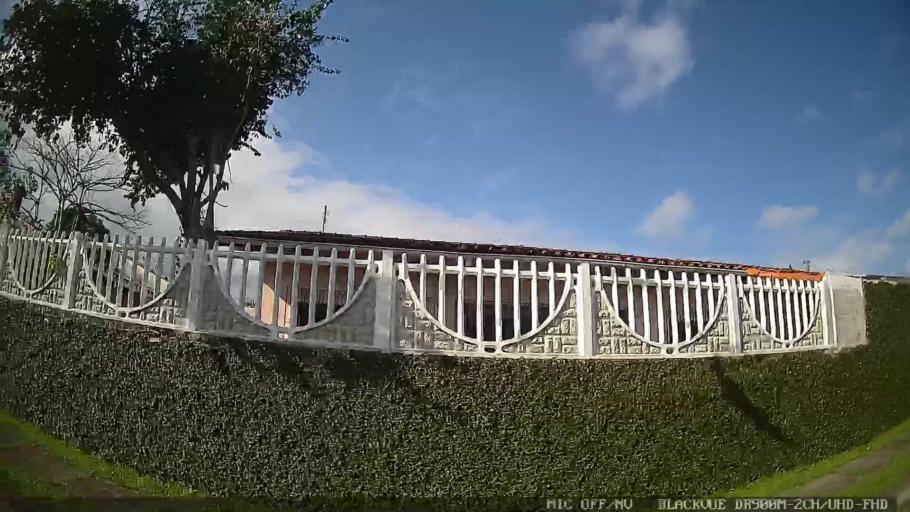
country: BR
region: Sao Paulo
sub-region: Peruibe
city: Peruibe
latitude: -24.3144
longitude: -46.9926
